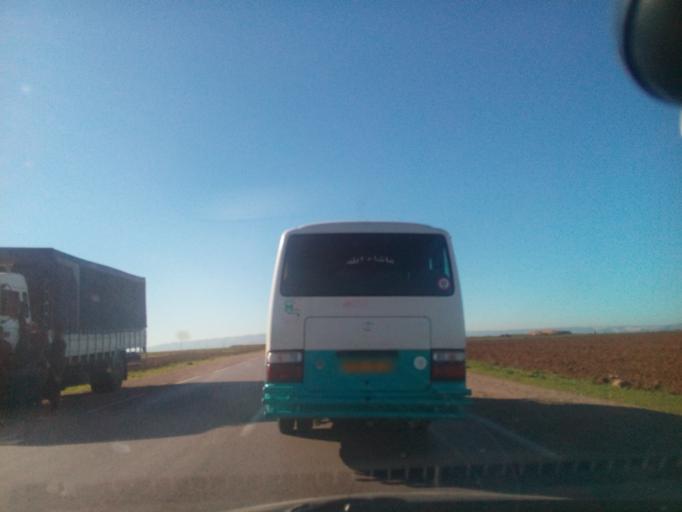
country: DZ
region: Relizane
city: Relizane
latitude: 35.8929
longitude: 0.6364
